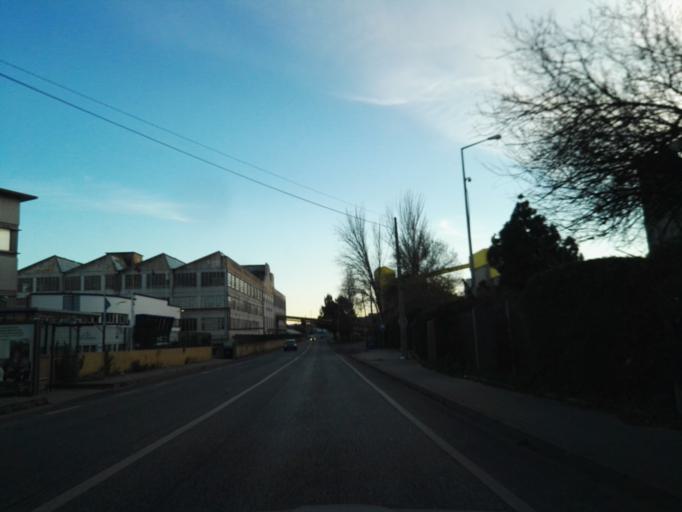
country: PT
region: Lisbon
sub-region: Loures
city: Santa Iria da Azoia
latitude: 38.8343
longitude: -9.0848
